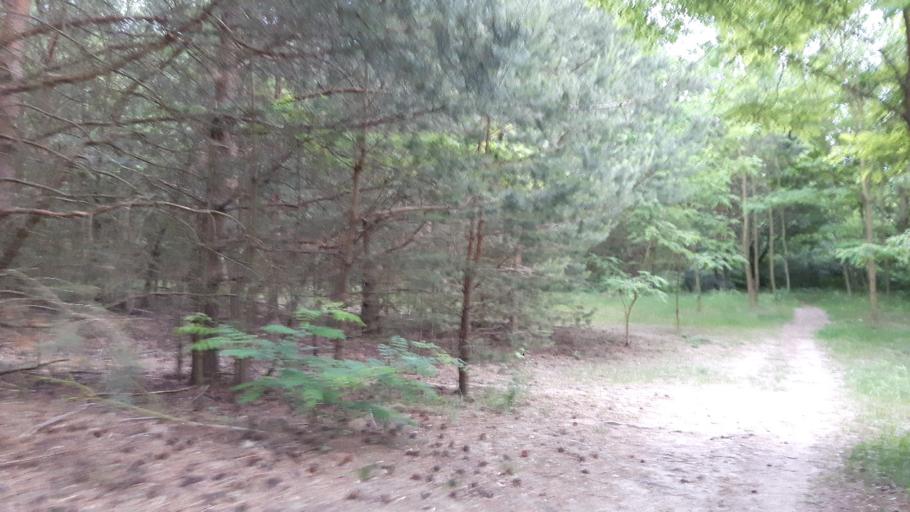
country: DE
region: Berlin
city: Wannsee
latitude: 52.4065
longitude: 13.1759
